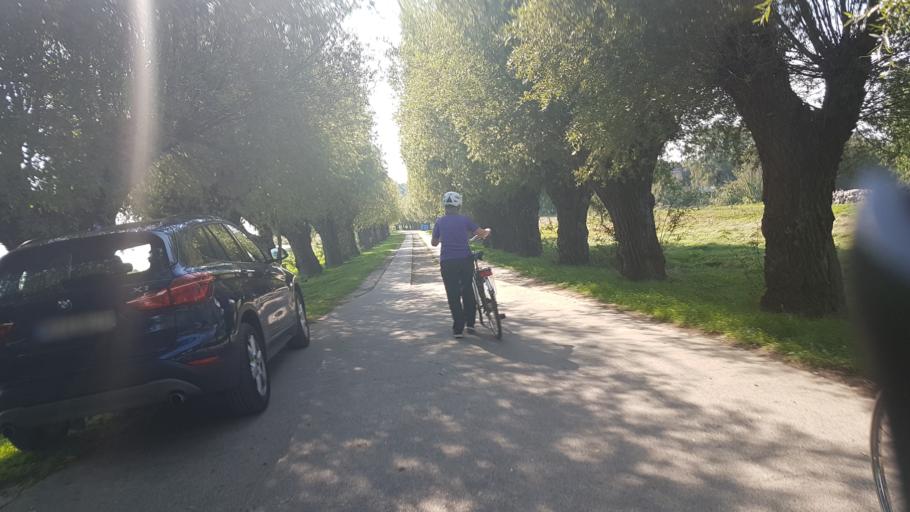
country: DE
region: Mecklenburg-Vorpommern
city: Putbus
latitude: 54.3357
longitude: 13.4837
